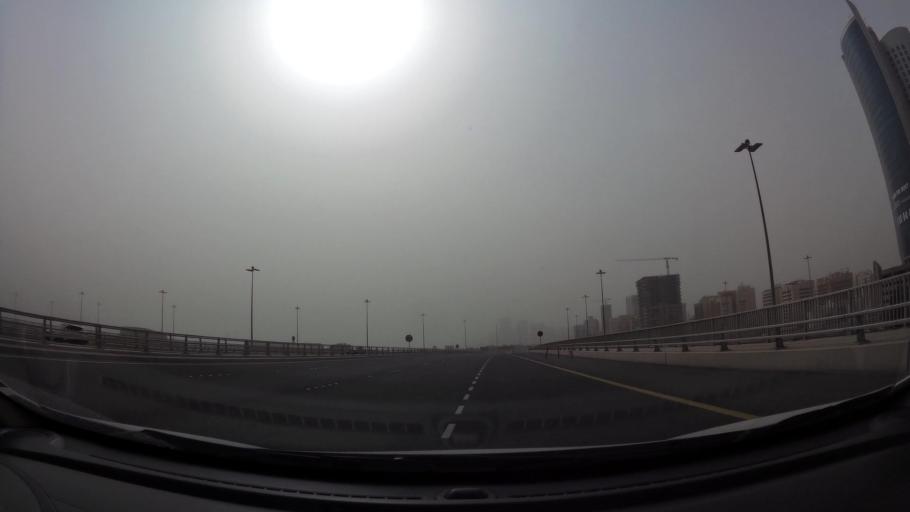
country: BH
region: Muharraq
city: Al Muharraq
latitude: 26.2431
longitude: 50.5931
